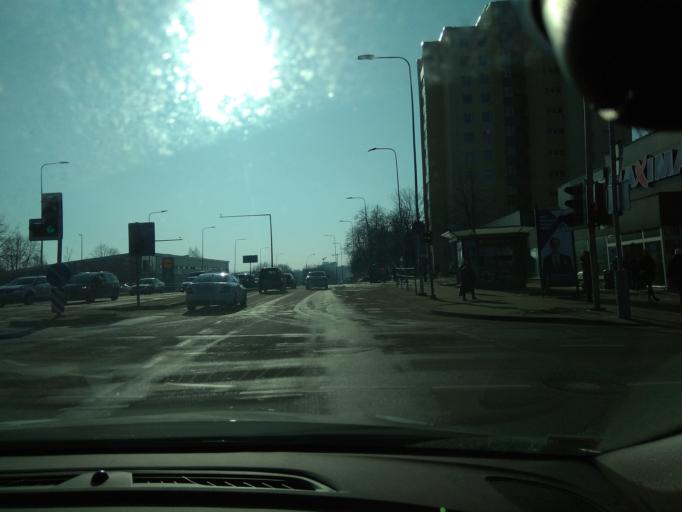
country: LT
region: Vilnius County
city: Naujamiestis
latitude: 54.6615
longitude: 25.2733
